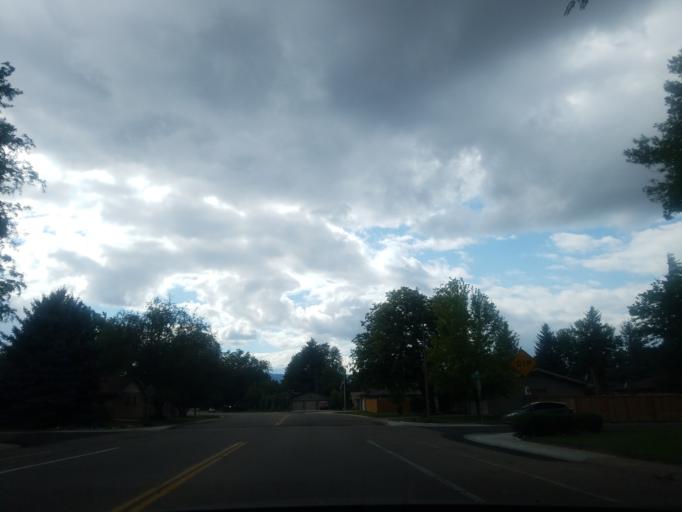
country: US
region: Colorado
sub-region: Larimer County
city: Fort Collins
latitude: 40.5579
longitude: -105.0735
